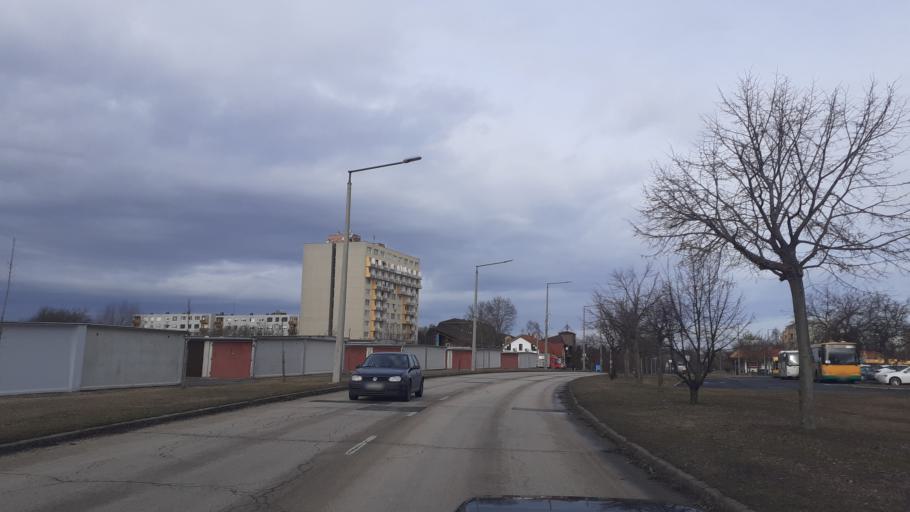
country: HU
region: Fejer
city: dunaujvaros
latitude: 46.9648
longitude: 18.9157
